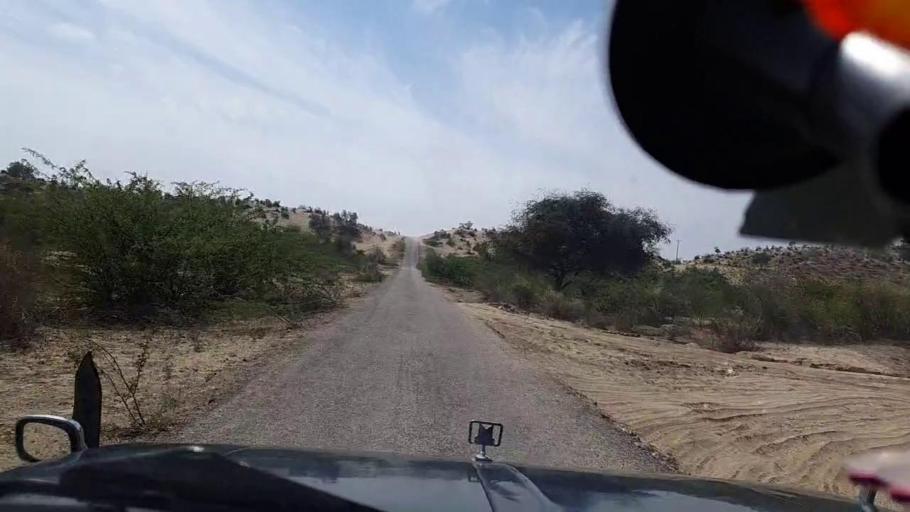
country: PK
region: Sindh
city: Diplo
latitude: 24.4158
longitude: 69.5848
